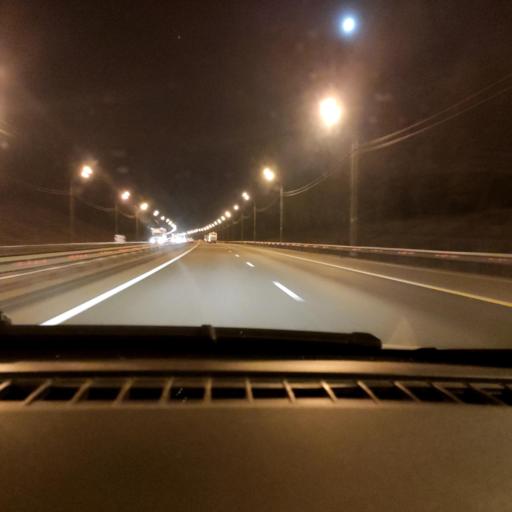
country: RU
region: Lipetsk
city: Khlevnoye
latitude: 52.2236
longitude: 39.1098
